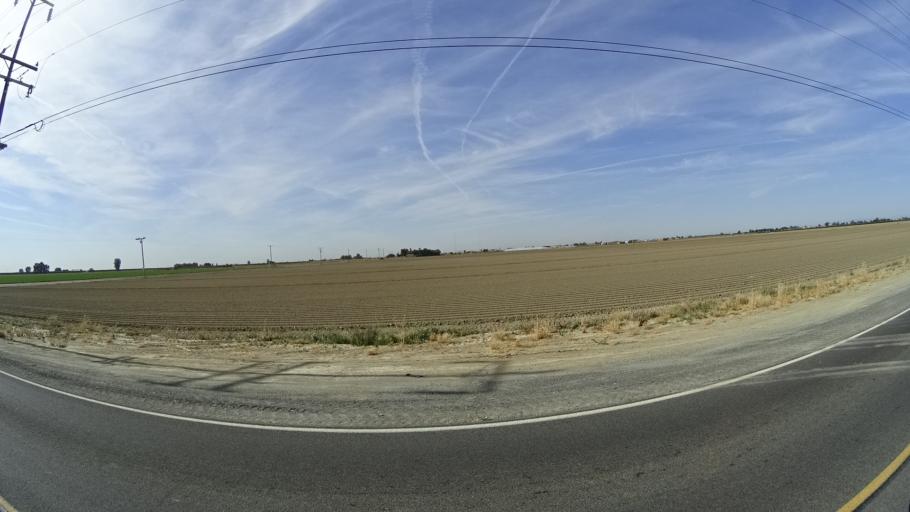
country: US
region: California
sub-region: Kings County
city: Home Garden
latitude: 36.3428
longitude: -119.5662
